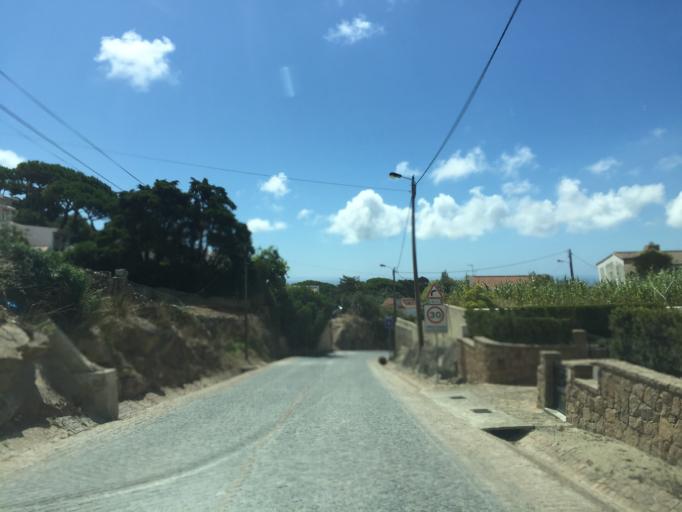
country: PT
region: Lisbon
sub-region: Cascais
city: Alcabideche
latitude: 38.7550
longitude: -9.4466
